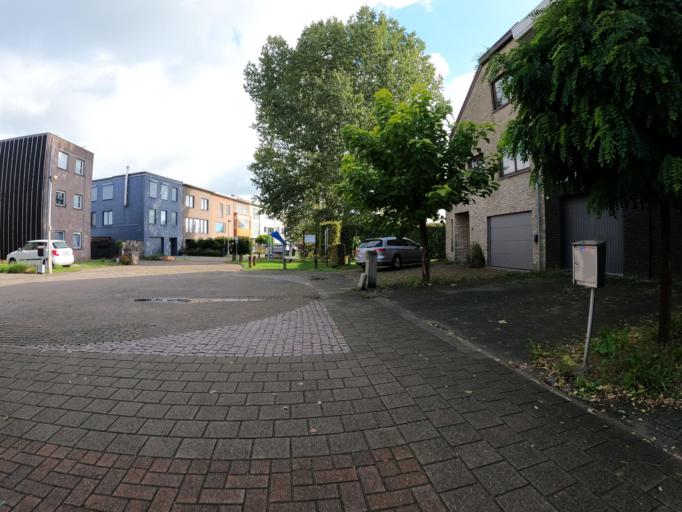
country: BE
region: Flanders
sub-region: Provincie Antwerpen
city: Wommelgem
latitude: 51.1777
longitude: 4.5290
